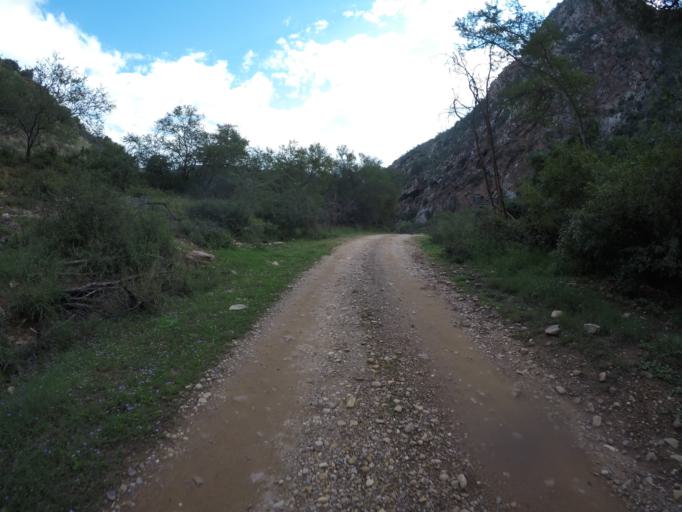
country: ZA
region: Eastern Cape
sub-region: Cacadu District Municipality
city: Kareedouw
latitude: -33.6362
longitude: 24.3196
